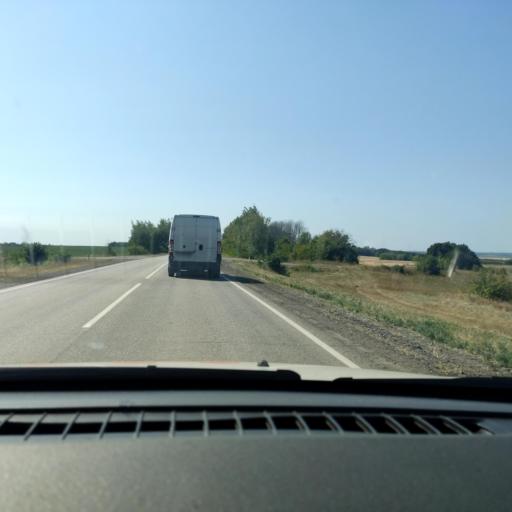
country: RU
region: Voronezj
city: Ostrogozhsk
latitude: 50.8024
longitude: 39.3194
